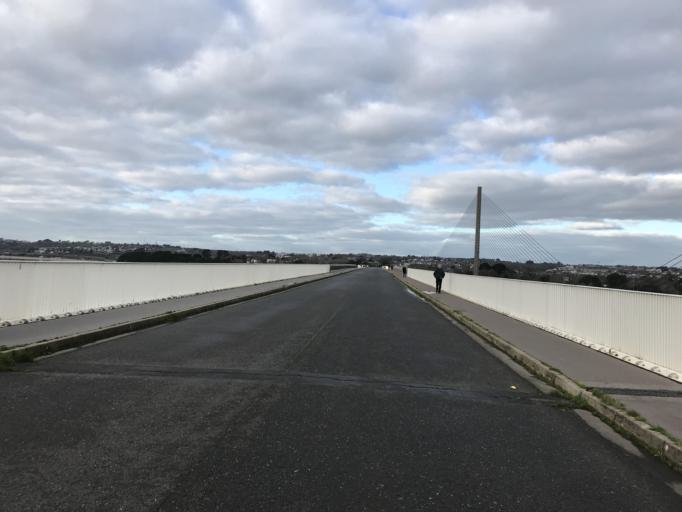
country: FR
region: Brittany
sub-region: Departement du Finistere
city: Le Relecq-Kerhuon
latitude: 48.3854
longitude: -4.3981
